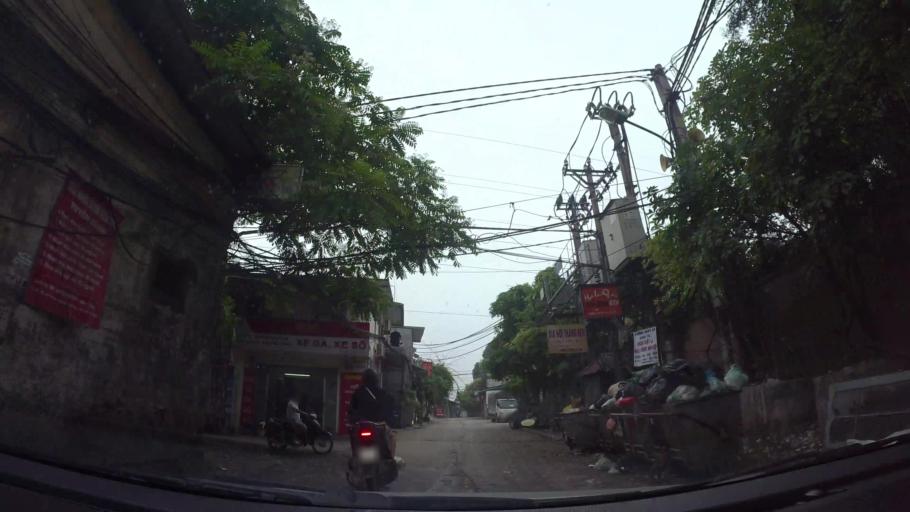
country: VN
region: Ha Noi
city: Hoan Kiem
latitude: 21.0558
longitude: 105.8414
